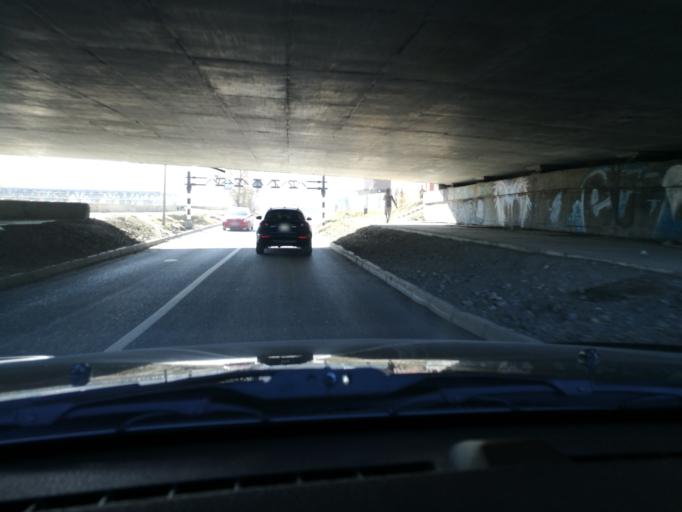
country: MN
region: Ulaanbaatar
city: Ulaanbaatar
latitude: 47.9234
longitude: 106.9314
